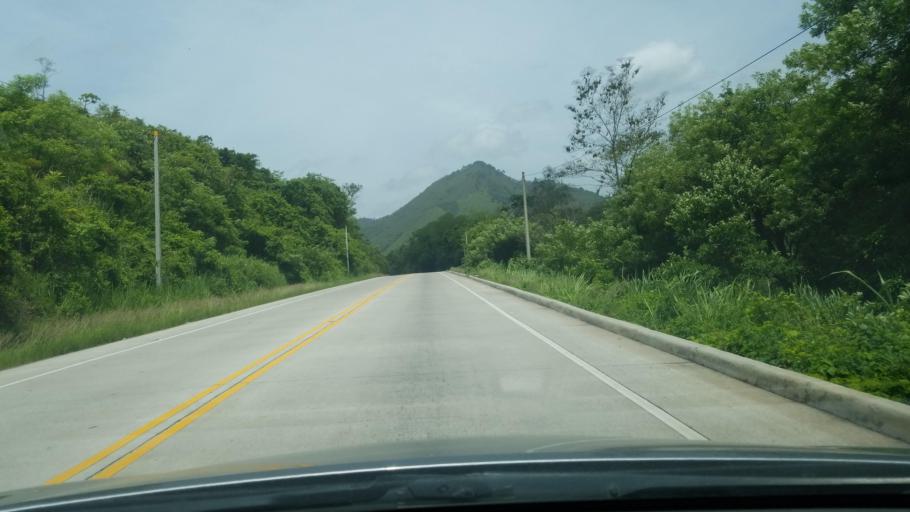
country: HN
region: Copan
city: Veracruz
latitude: 14.8890
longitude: -88.7658
